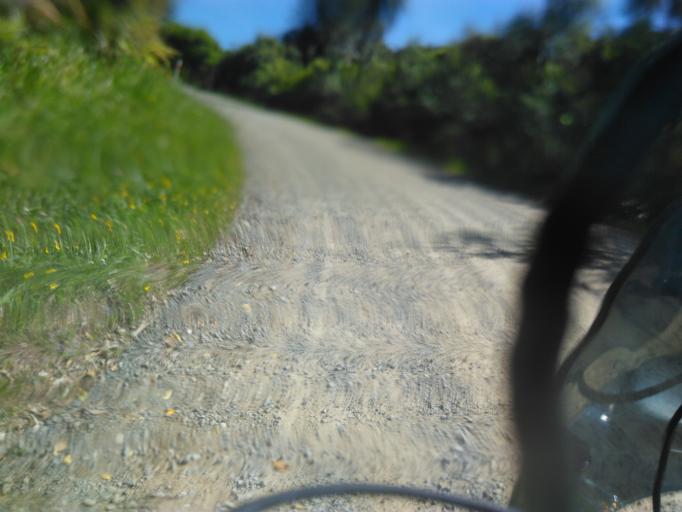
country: NZ
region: Hawke's Bay
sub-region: Wairoa District
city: Wairoa
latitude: -38.7971
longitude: 177.1254
